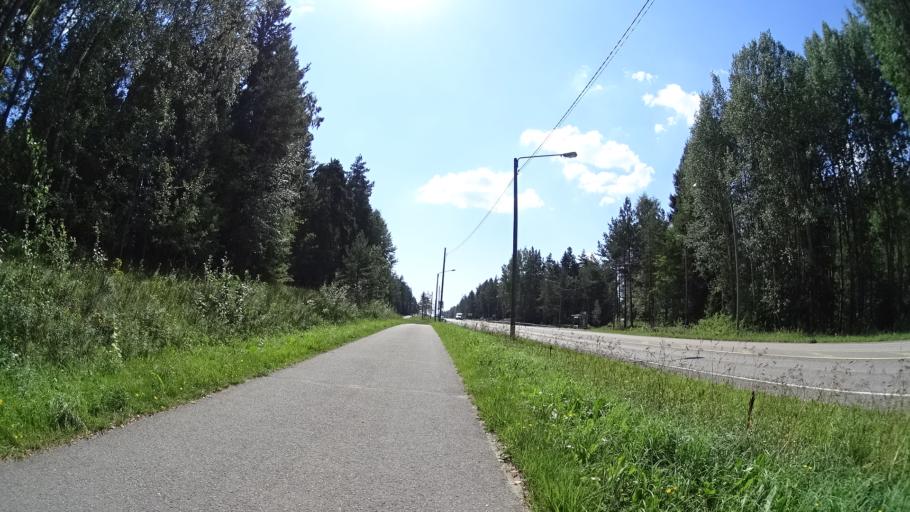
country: FI
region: Uusimaa
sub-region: Helsinki
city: Vantaa
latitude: 60.3200
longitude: 25.0010
